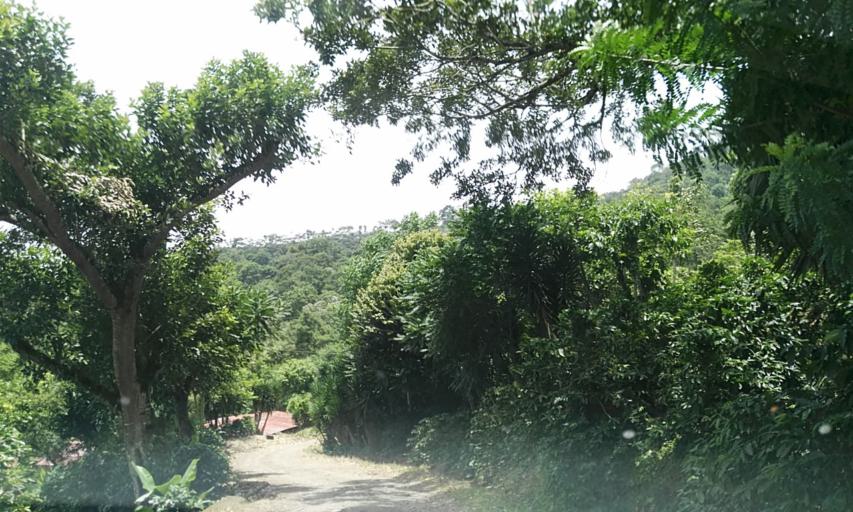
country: NI
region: Matagalpa
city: San Ramon
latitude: 13.0091
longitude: -85.8752
